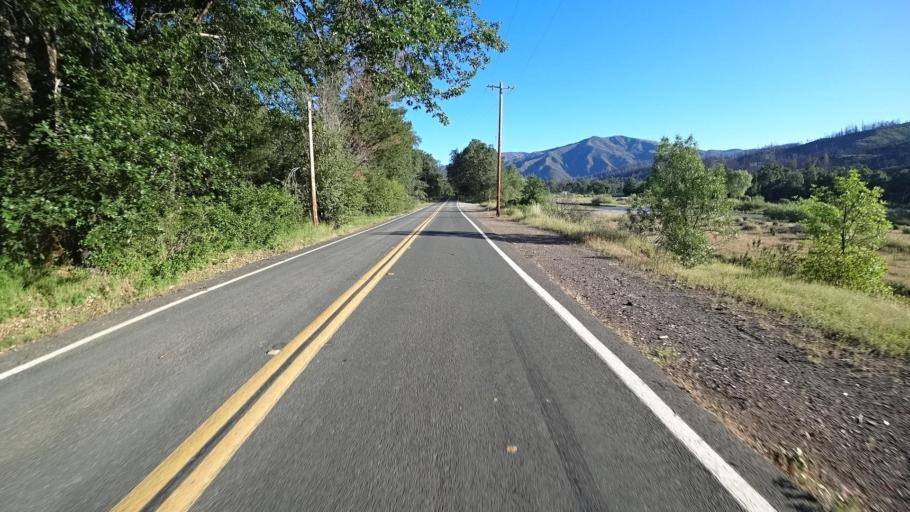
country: US
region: California
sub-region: Lake County
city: Upper Lake
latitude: 39.2302
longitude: -122.9443
